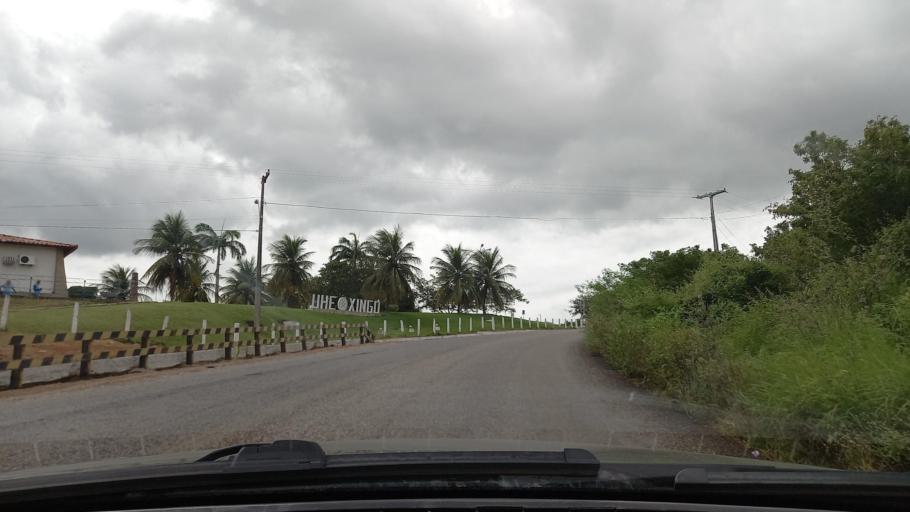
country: BR
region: Sergipe
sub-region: Caninde De Sao Francisco
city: Caninde de Sao Francisco
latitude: -9.6303
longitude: -37.7848
